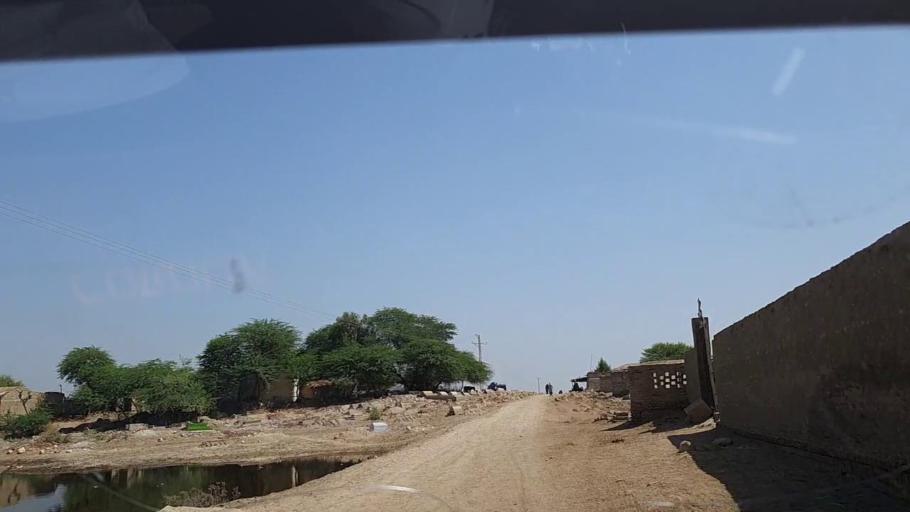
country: PK
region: Sindh
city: Ghauspur
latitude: 28.1349
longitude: 69.0853
